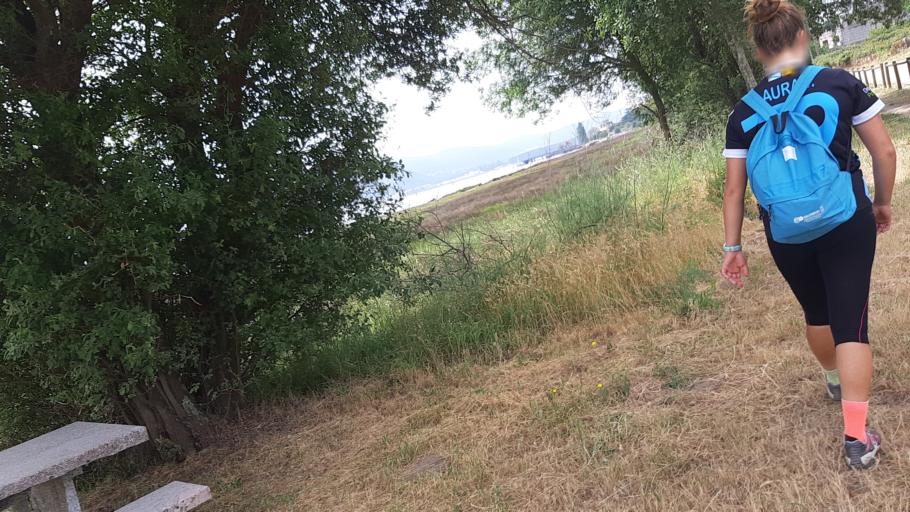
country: ES
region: Galicia
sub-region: Provincia de Pontevedra
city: A Guarda
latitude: 41.8964
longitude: -8.8493
